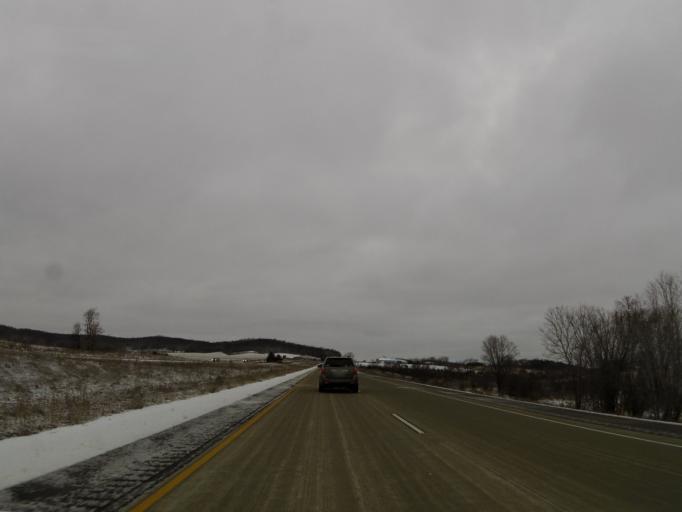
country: US
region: Wisconsin
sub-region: Trempealeau County
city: Osseo
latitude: 44.6220
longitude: -91.2637
